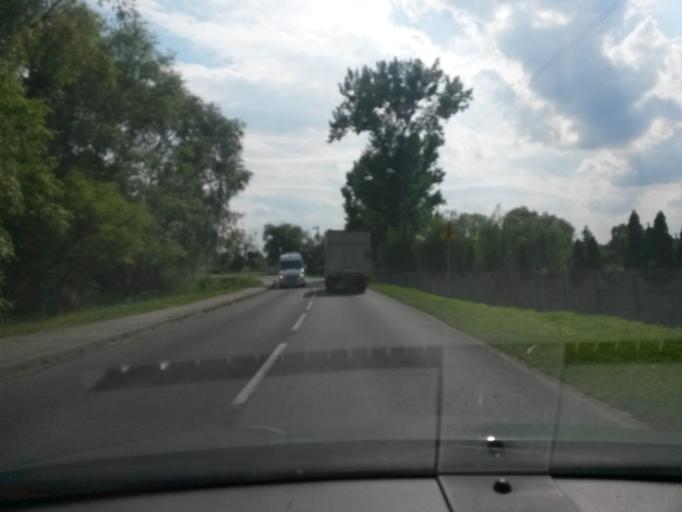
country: PL
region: Greater Poland Voivodeship
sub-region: Powiat poznanski
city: Kleszczewo
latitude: 52.3008
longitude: 17.1240
